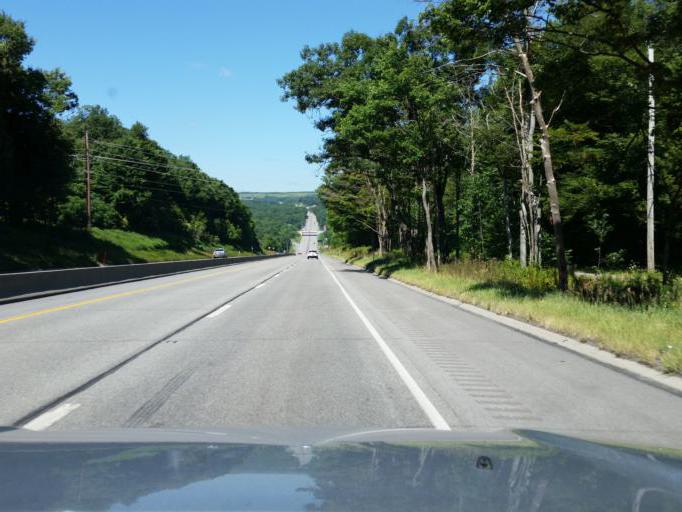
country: US
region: Pennsylvania
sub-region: Cambria County
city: Mundys Corner
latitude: 40.4486
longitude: -78.8240
